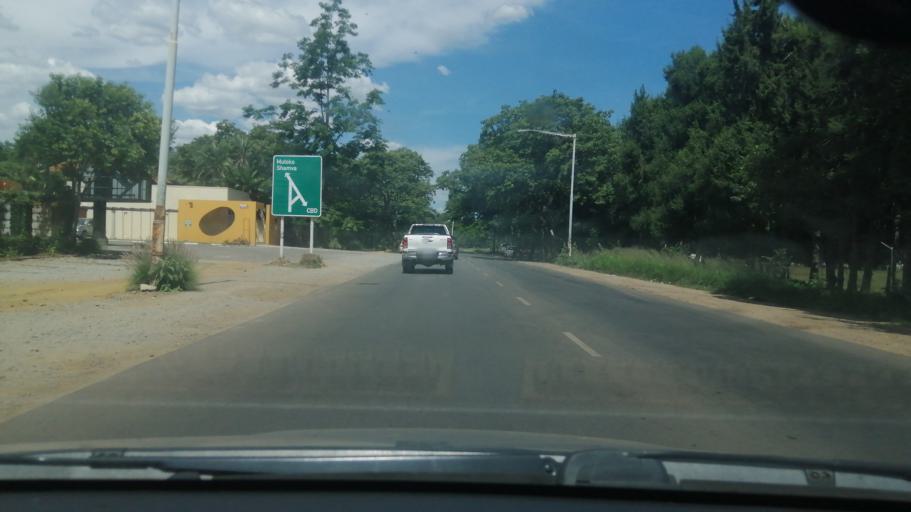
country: ZW
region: Harare
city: Harare
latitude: -17.8184
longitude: 31.0626
